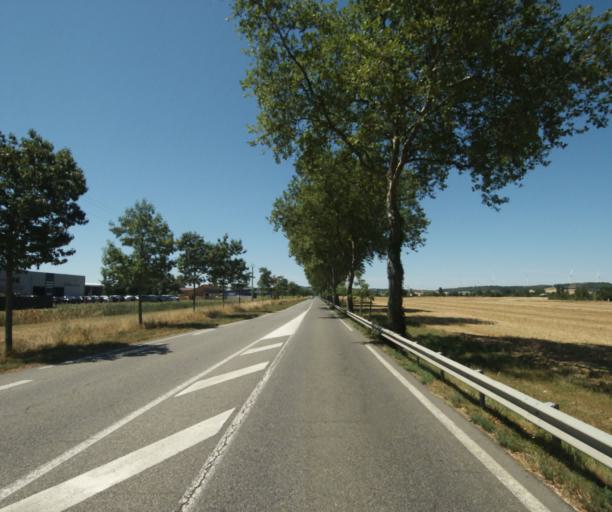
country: FR
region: Midi-Pyrenees
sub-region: Departement de la Haute-Garonne
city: Saint-Felix-Lauragais
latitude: 43.4462
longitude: 1.9447
